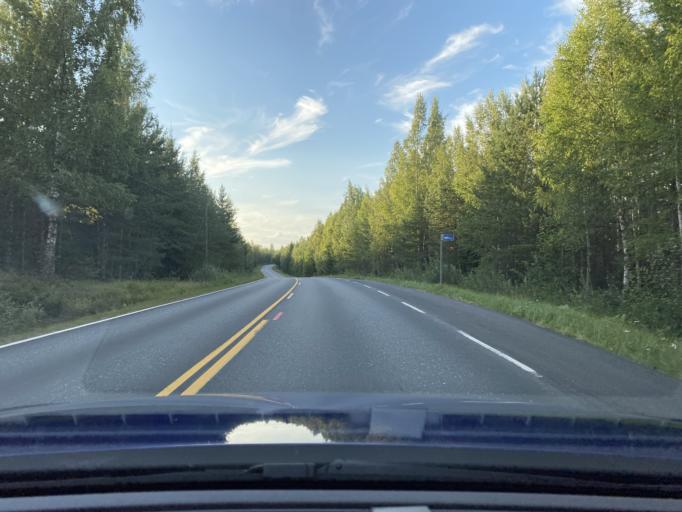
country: FI
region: Pirkanmaa
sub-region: Lounais-Pirkanmaa
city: Punkalaidun
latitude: 61.1784
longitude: 23.0568
